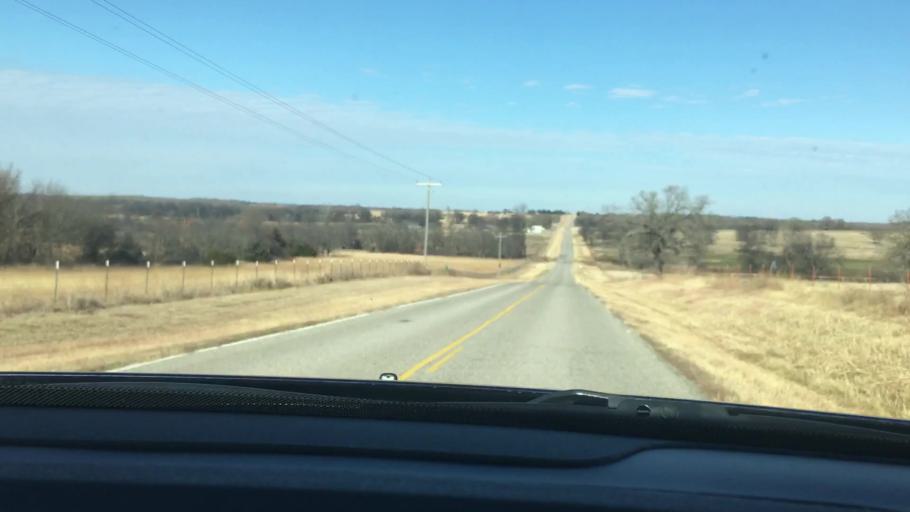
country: US
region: Oklahoma
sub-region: Garvin County
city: Wynnewood
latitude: 34.6737
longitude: -97.1254
